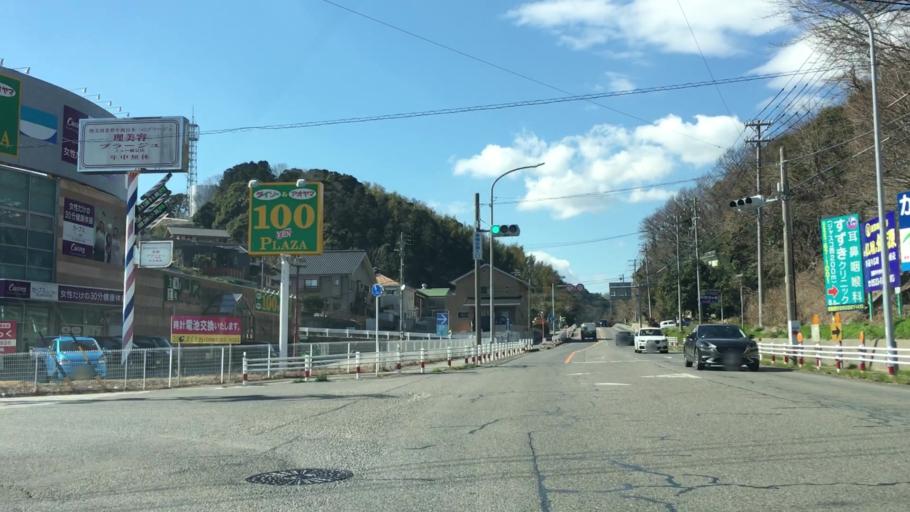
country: JP
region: Aichi
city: Nishio
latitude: 34.7948
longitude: 137.1316
